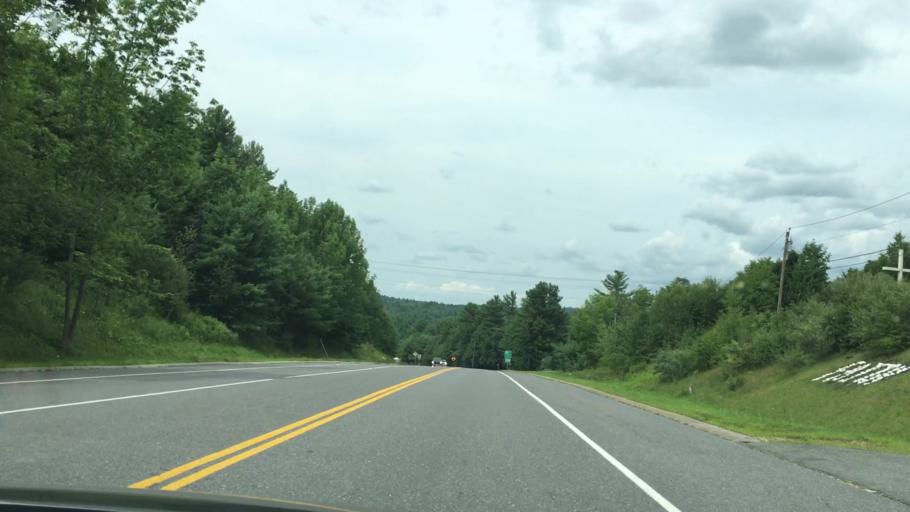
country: US
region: Massachusetts
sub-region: Worcester County
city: Gardner
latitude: 42.5995
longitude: -71.9884
